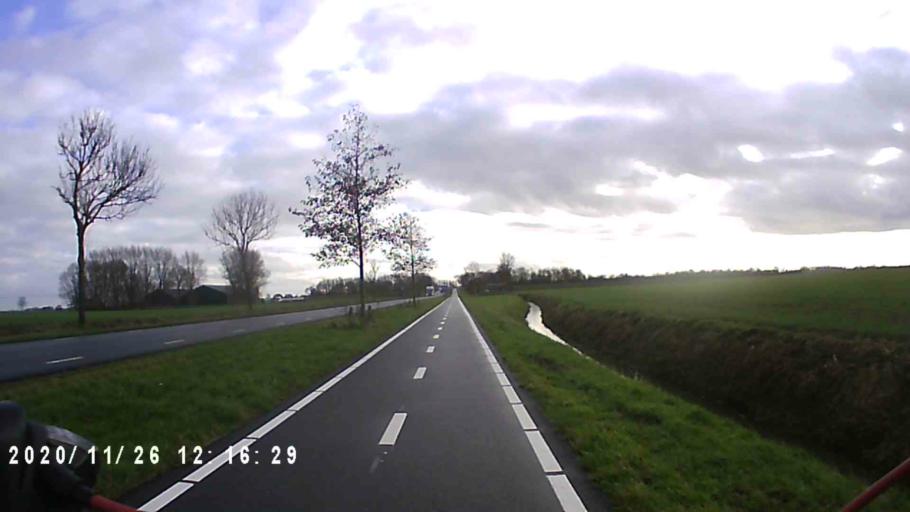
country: NL
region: Groningen
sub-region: Gemeente Bedum
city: Bedum
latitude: 53.3365
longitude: 6.6642
